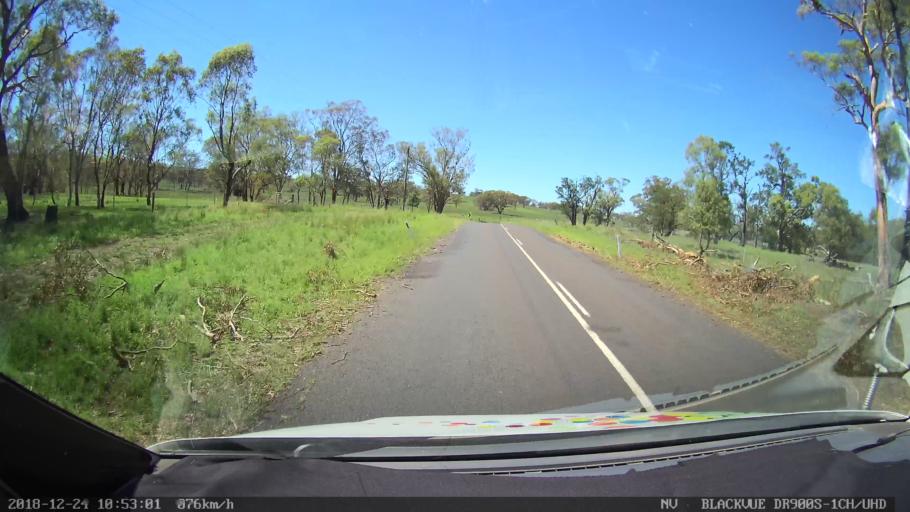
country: AU
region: New South Wales
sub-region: Upper Hunter Shire
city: Merriwa
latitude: -31.9873
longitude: 150.4229
